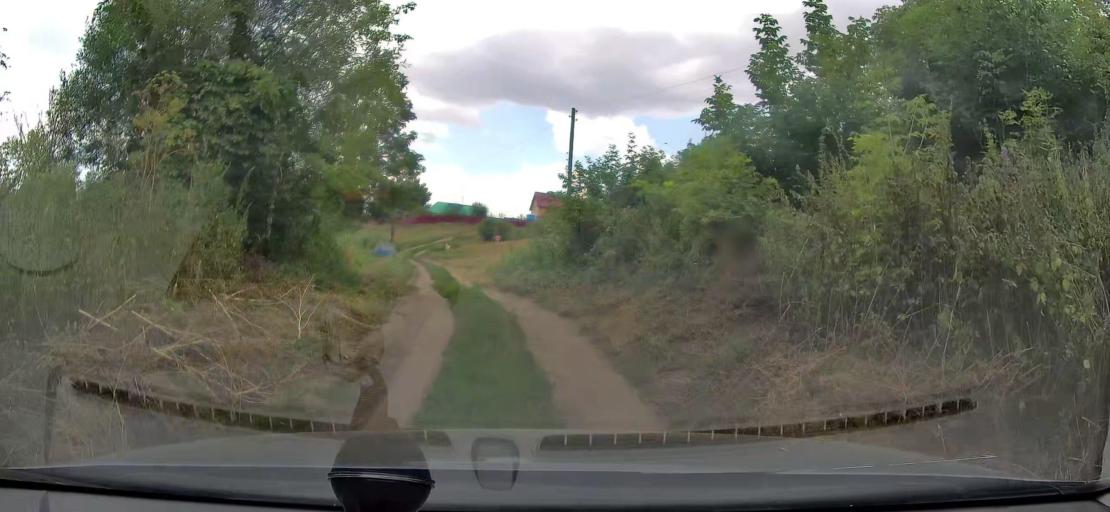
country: RU
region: Kursk
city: Zolotukhino
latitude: 52.0295
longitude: 36.2009
